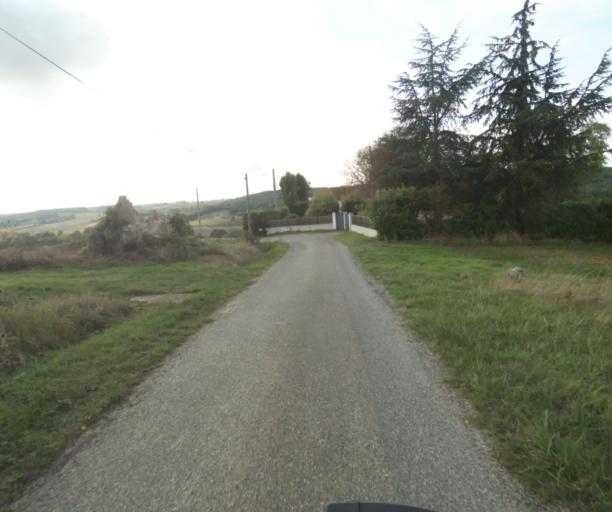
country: FR
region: Midi-Pyrenees
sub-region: Departement de la Haute-Garonne
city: Launac
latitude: 43.8073
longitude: 1.1212
